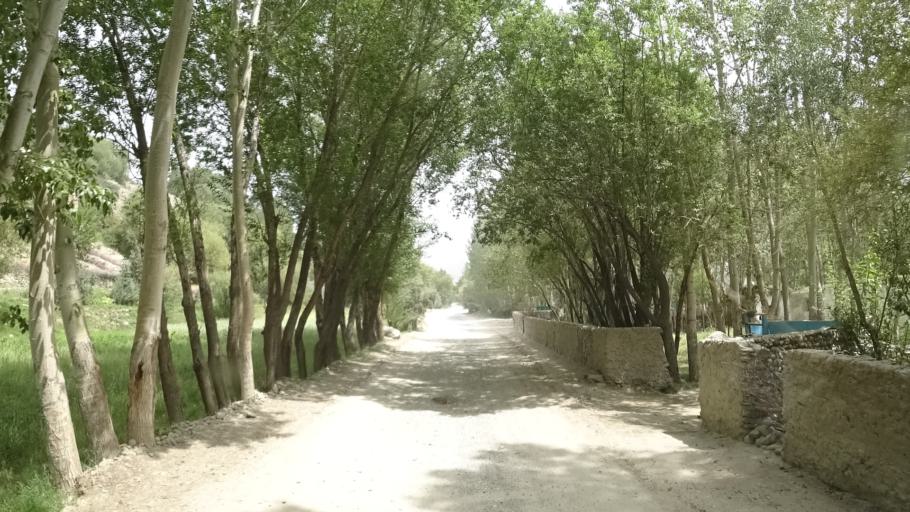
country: AF
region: Badakhshan
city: Khandud
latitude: 37.0464
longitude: 72.6696
